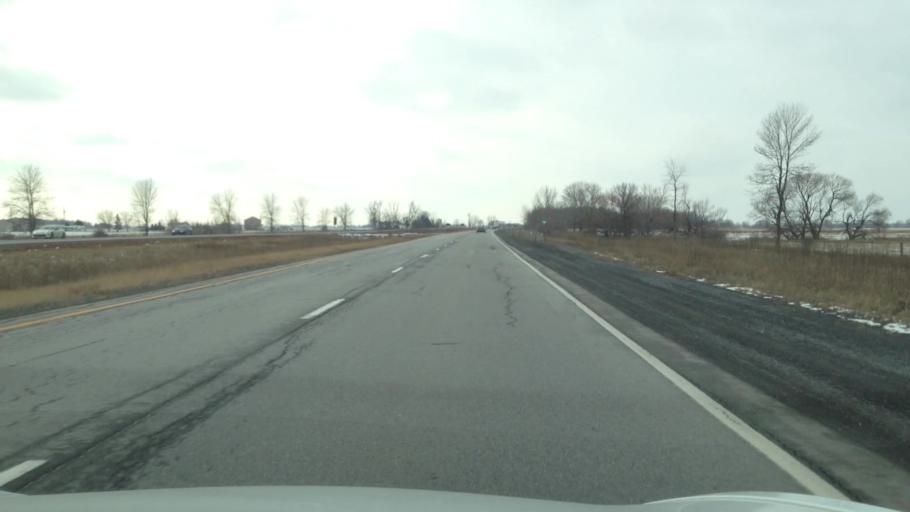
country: CA
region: Ontario
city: Casselman
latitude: 45.3179
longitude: -75.0184
